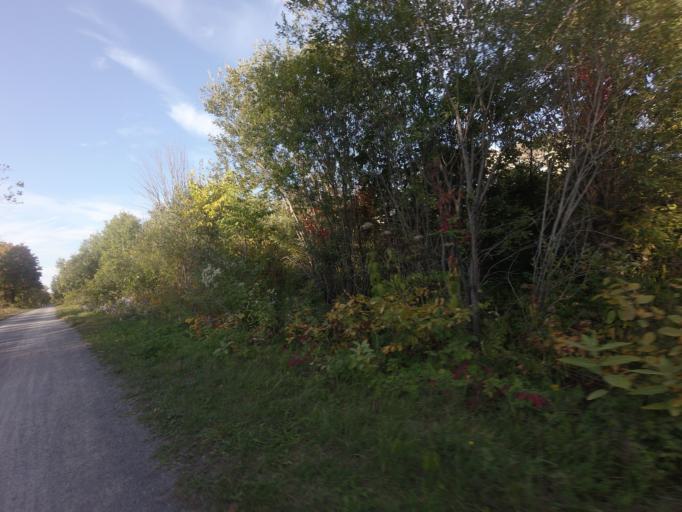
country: CA
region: Quebec
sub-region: Laurentides
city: Prevost
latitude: 45.8389
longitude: -74.0592
